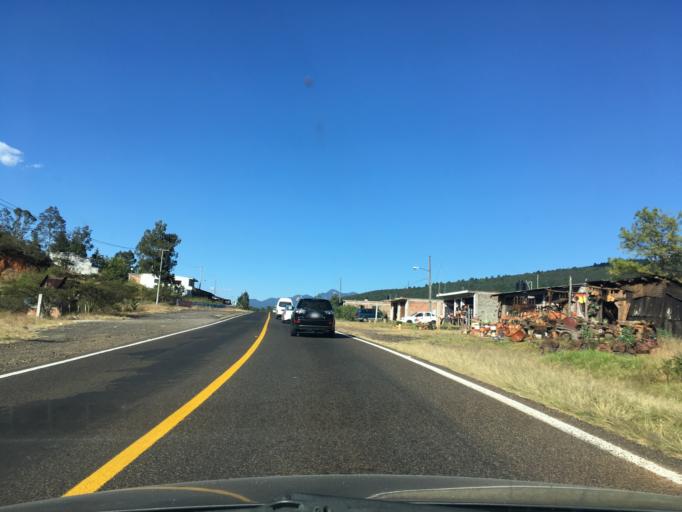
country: MX
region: Michoacan
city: Tzintzuntzan
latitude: 19.5998
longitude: -101.5741
